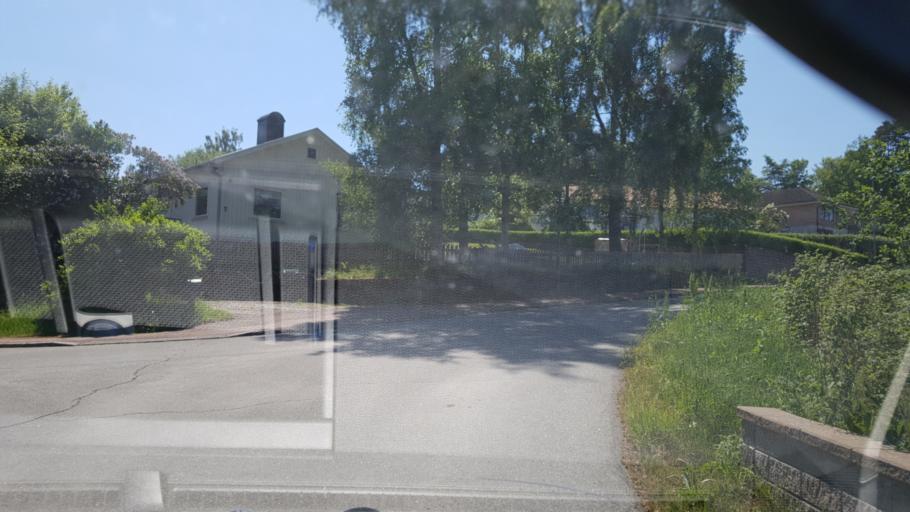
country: SE
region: Vaestra Goetaland
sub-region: Lerums Kommun
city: Stenkullen
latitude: 57.8047
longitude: 12.3585
